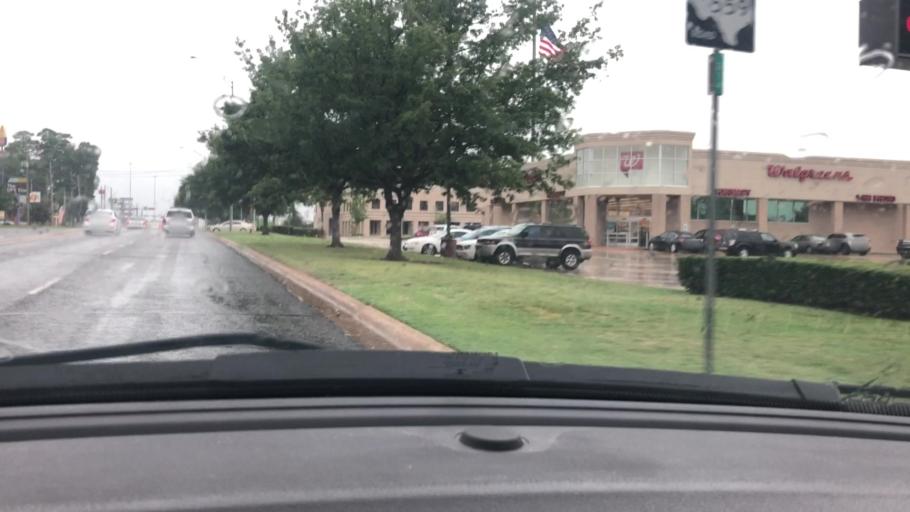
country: US
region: Texas
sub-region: Bowie County
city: Wake Village
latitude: 33.4522
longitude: -94.0803
